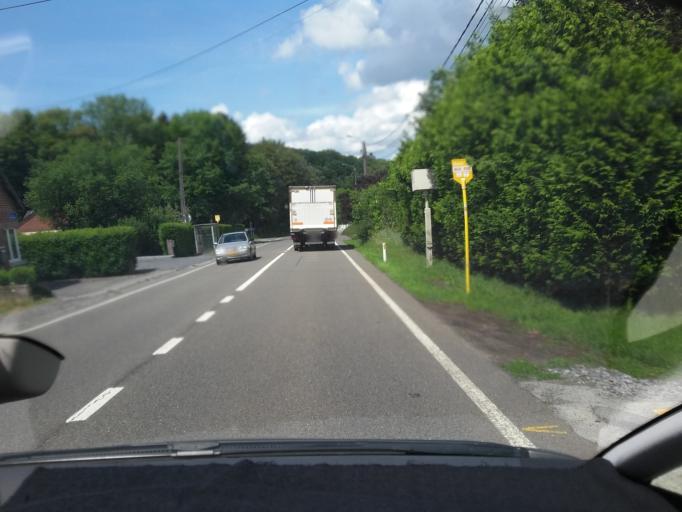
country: BE
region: Wallonia
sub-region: Province de Namur
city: Rochefort
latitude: 50.1445
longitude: 5.2204
